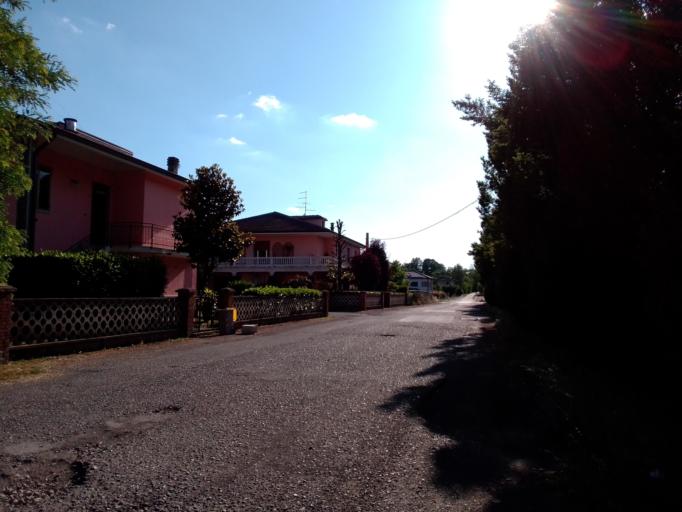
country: IT
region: Emilia-Romagna
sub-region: Provincia di Piacenza
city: Borgonovo Valtidone
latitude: 45.0073
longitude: 9.4432
